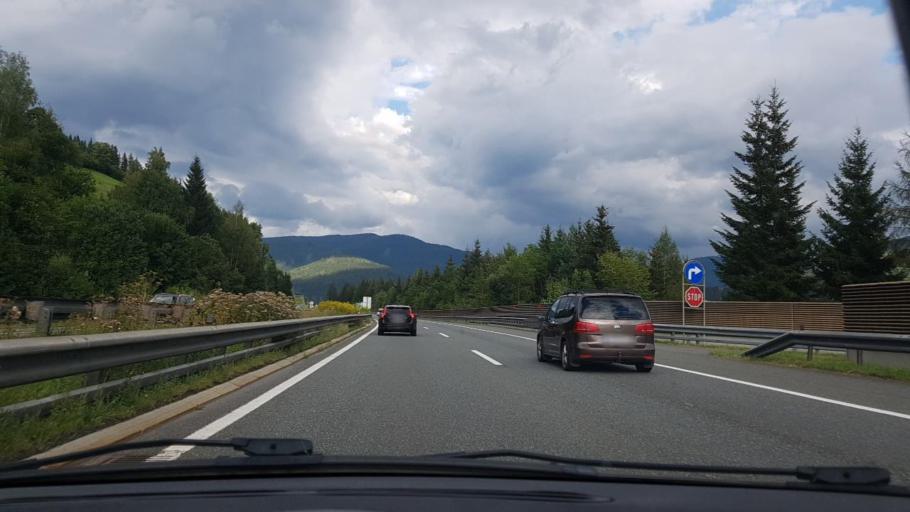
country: AT
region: Salzburg
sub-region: Politischer Bezirk Sankt Johann im Pongau
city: Huttau
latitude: 47.4190
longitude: 13.3195
